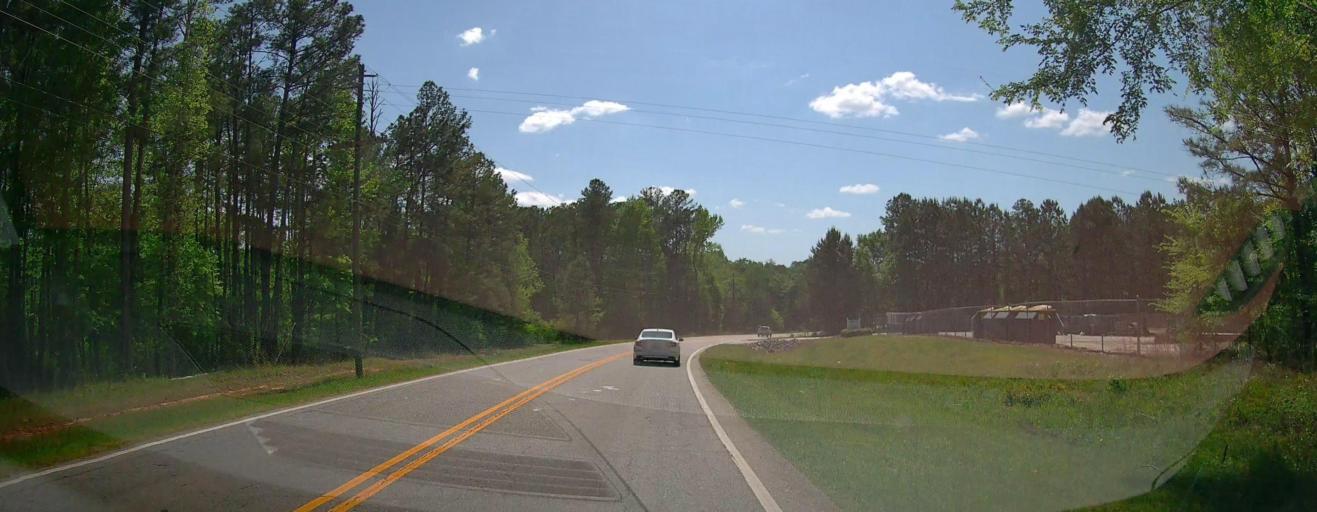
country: US
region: Georgia
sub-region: Putnam County
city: Eatonton
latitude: 33.2394
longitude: -83.3094
